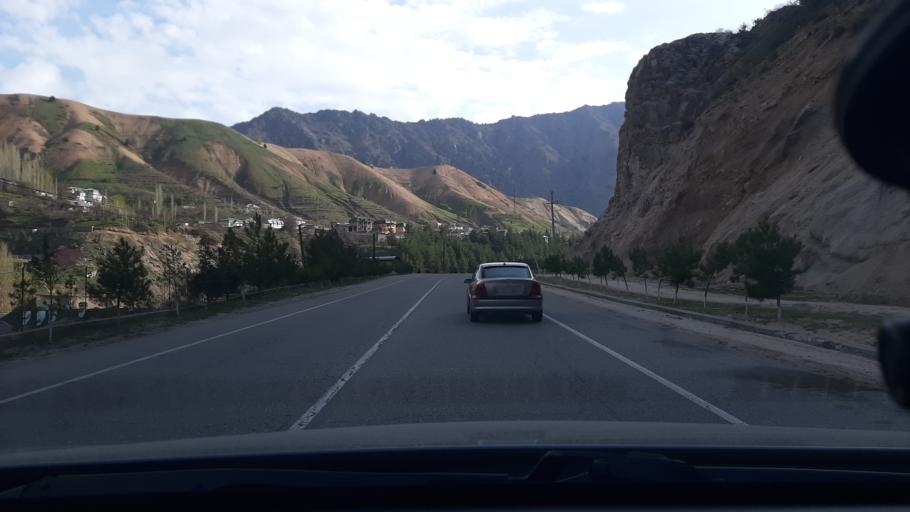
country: TJ
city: Tagob
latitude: 38.8428
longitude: 68.8346
